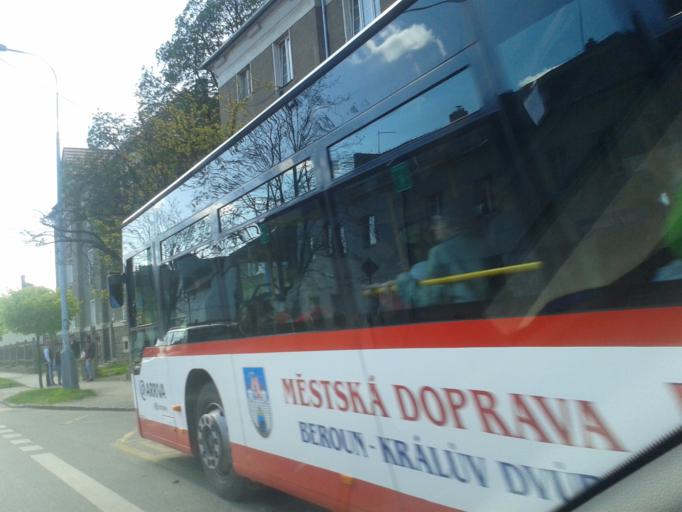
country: CZ
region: Central Bohemia
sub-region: Okres Beroun
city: Beroun
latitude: 49.9608
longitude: 14.0598
